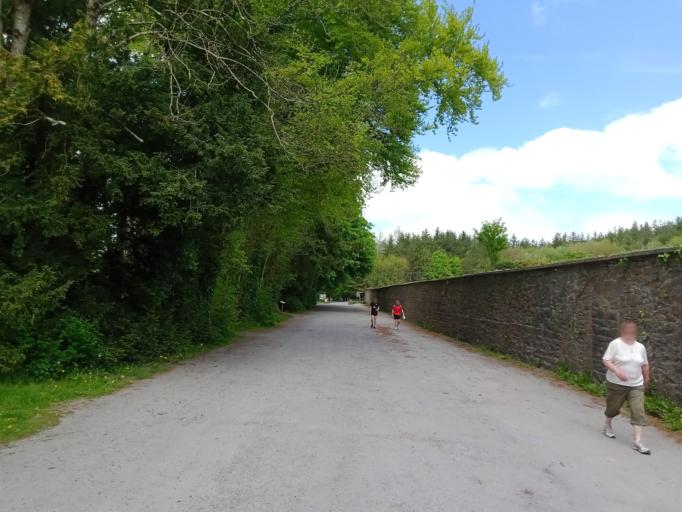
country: IE
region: Leinster
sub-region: Kilkenny
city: Castlecomer
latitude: 52.8079
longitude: -7.2032
